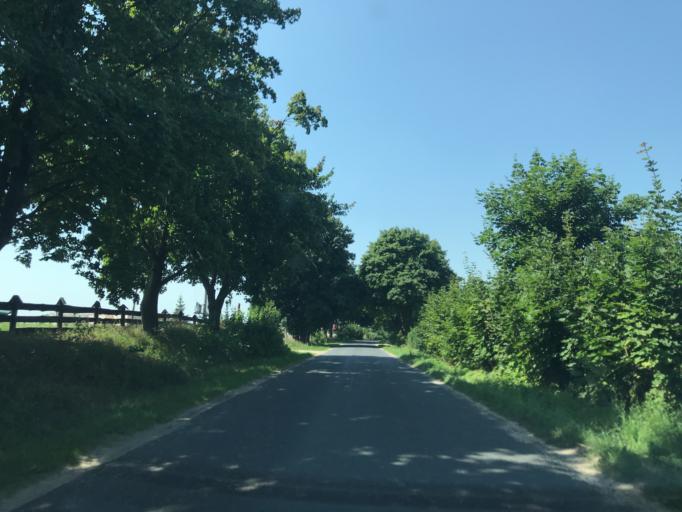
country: PL
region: Kujawsko-Pomorskie
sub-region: Powiat lipnowski
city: Chrostkowo
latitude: 52.9958
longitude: 19.2256
